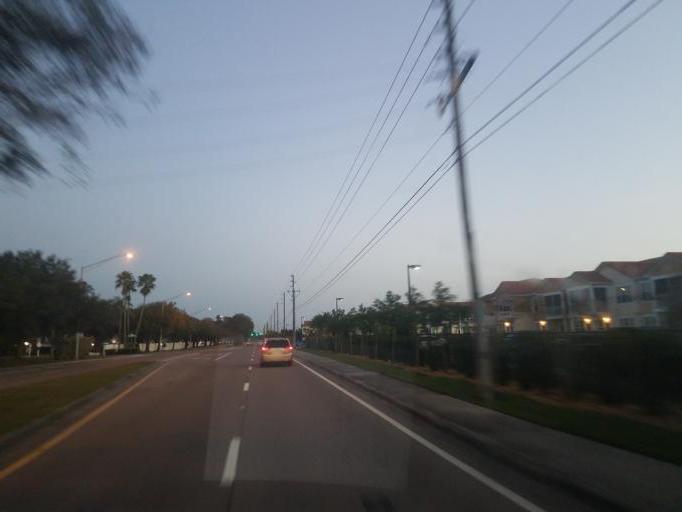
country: US
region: Florida
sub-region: Sarasota County
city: Lake Sarasota
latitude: 27.2857
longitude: -82.4522
